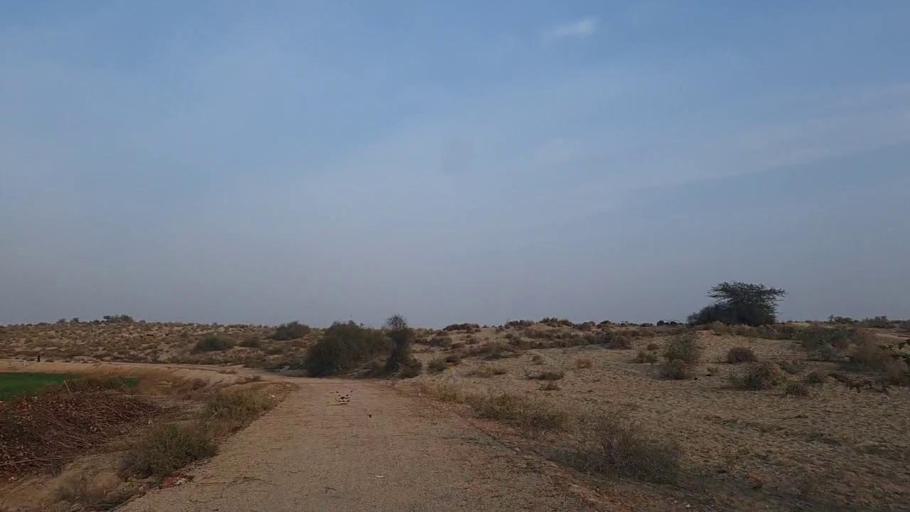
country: PK
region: Sindh
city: Jam Sahib
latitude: 26.4083
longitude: 68.6089
